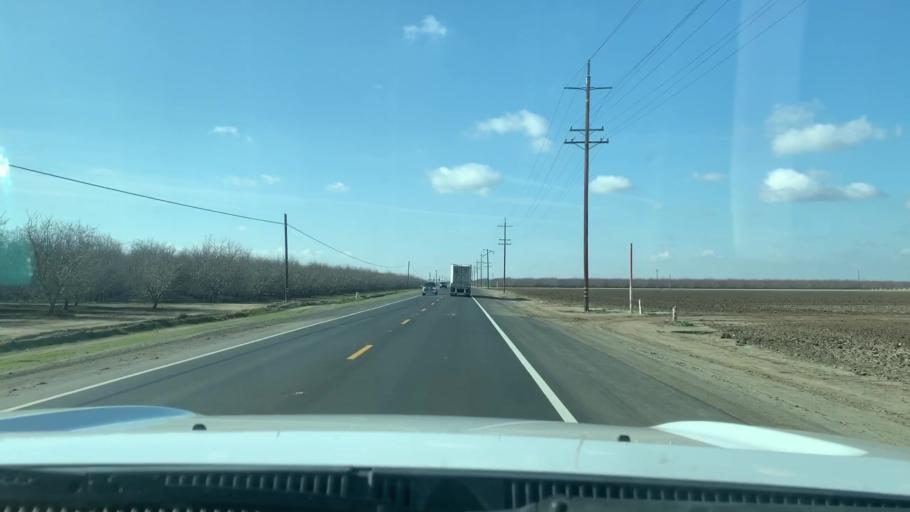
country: US
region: California
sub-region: Kern County
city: Wasco
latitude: 35.6017
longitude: -119.3075
